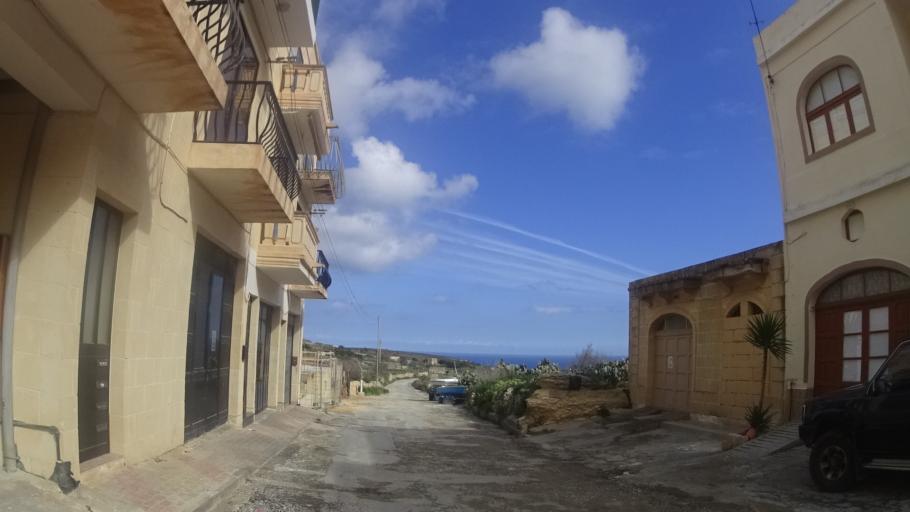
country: MT
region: In-Nadur
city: Nadur
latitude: 36.0425
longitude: 14.2986
